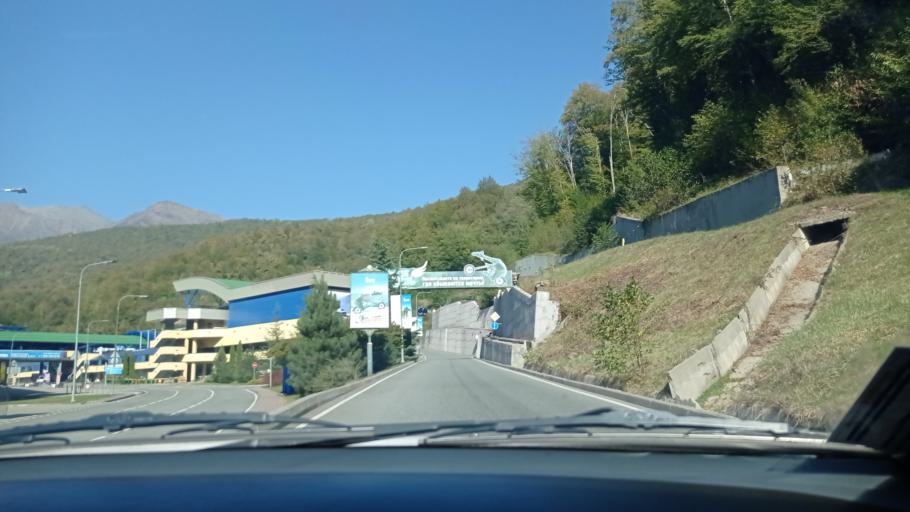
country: RU
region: Krasnodarskiy
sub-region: Sochi City
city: Krasnaya Polyana
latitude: 43.6827
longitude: 40.2802
